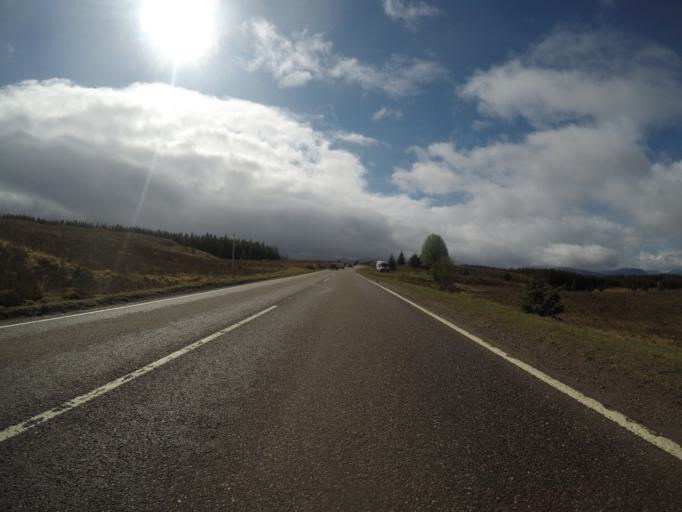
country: GB
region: Scotland
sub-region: Highland
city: Spean Bridge
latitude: 57.0976
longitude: -4.9951
